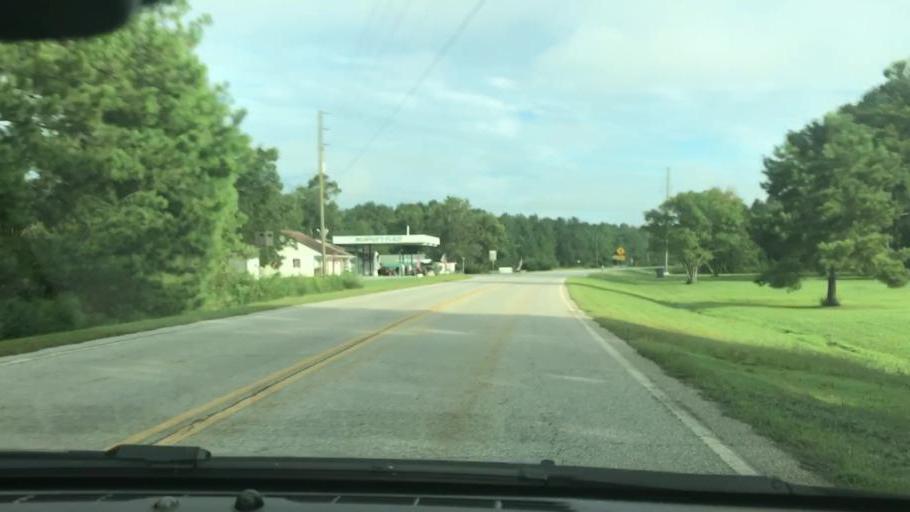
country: US
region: Georgia
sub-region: Quitman County
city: Georgetown
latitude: 31.7688
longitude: -85.0905
